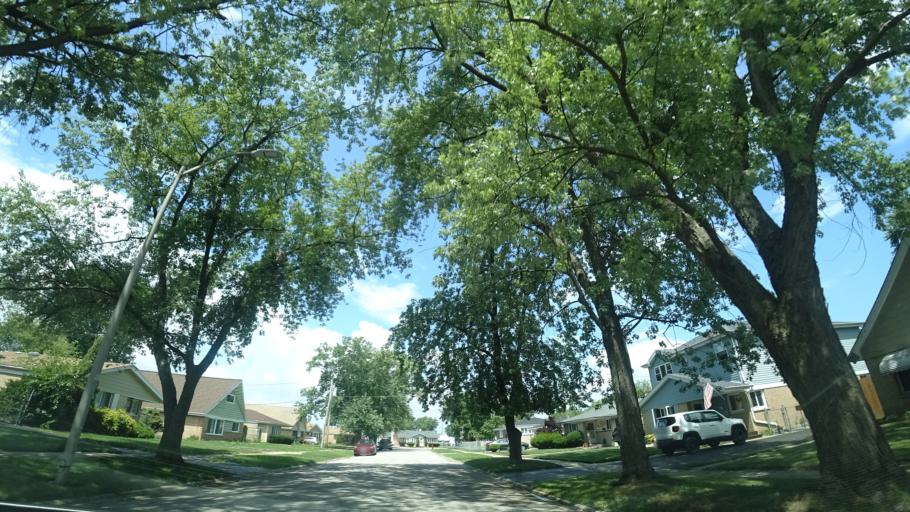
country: US
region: Illinois
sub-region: Cook County
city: Alsip
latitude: 41.6665
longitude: -87.7321
